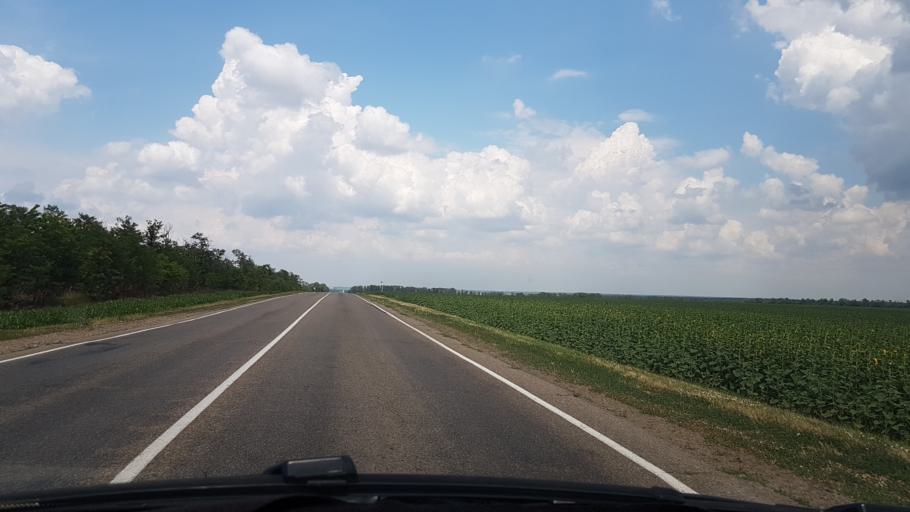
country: RU
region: Krasnodarskiy
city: Dmitriyevskaya
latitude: 45.6802
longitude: 40.7440
